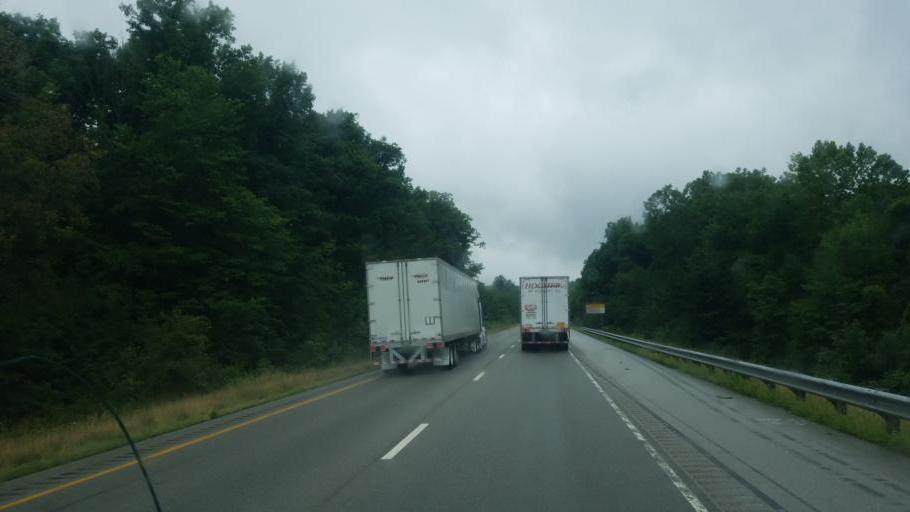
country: US
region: Indiana
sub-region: Putnam County
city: Cloverdale
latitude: 39.5412
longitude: -86.7513
